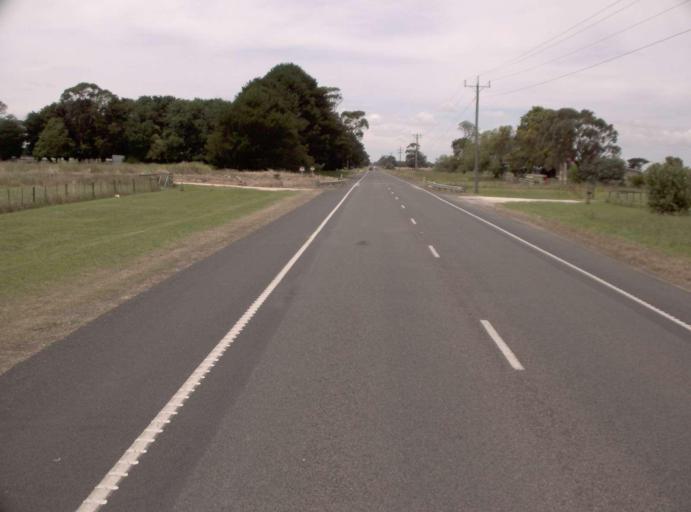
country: AU
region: Victoria
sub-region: Wellington
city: Sale
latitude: -38.0679
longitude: 147.0336
